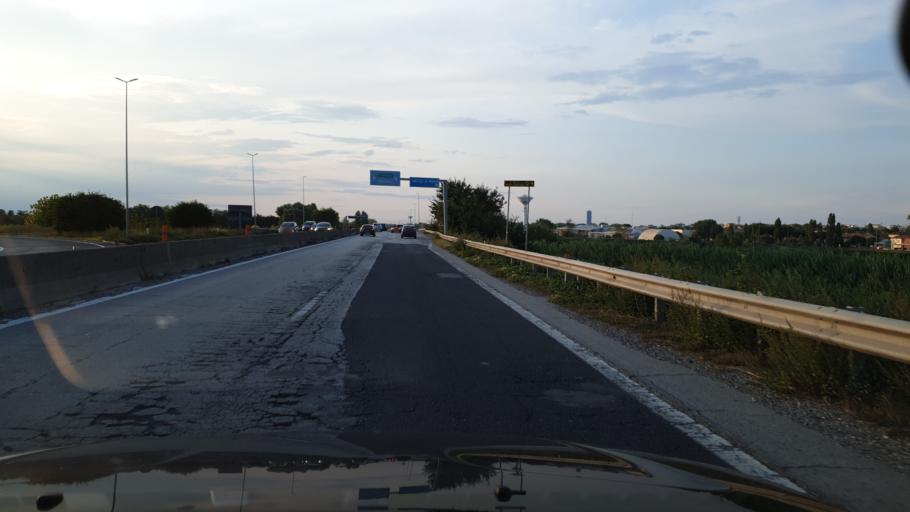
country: IT
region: Emilia-Romagna
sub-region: Forli-Cesena
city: Gatteo a Mare
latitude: 44.1676
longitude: 12.4247
